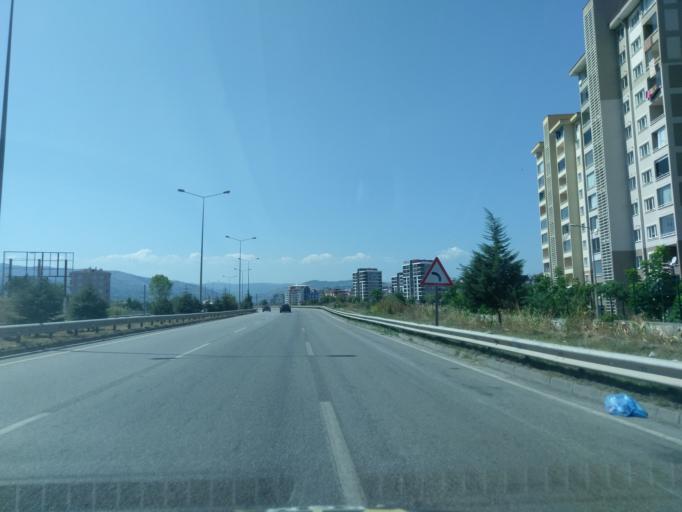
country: TR
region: Samsun
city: Samsun
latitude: 41.2636
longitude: 36.3454
